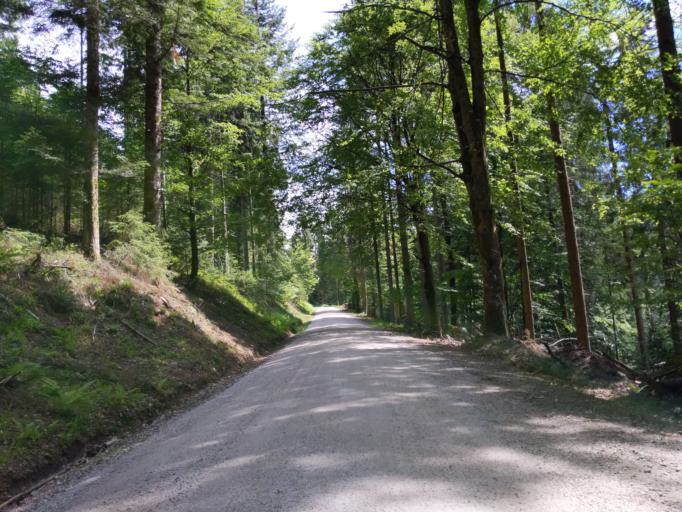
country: DE
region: Baden-Wuerttemberg
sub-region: Karlsruhe Region
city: Bad Rippoldsau-Schapbach
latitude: 48.4148
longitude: 8.3633
